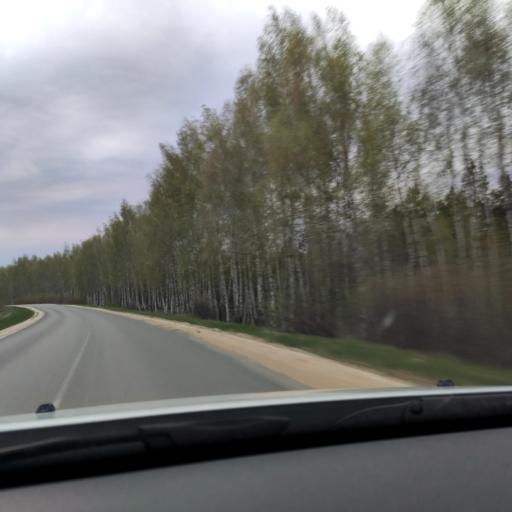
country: RU
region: Lipetsk
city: Donskoye
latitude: 52.6396
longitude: 38.9851
